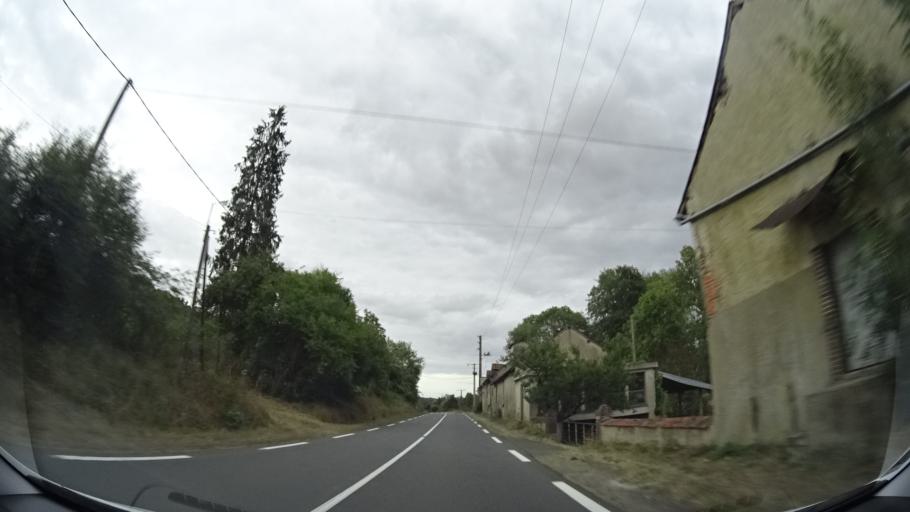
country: FR
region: Centre
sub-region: Departement du Loiret
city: Trigueres
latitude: 47.9446
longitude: 3.0091
